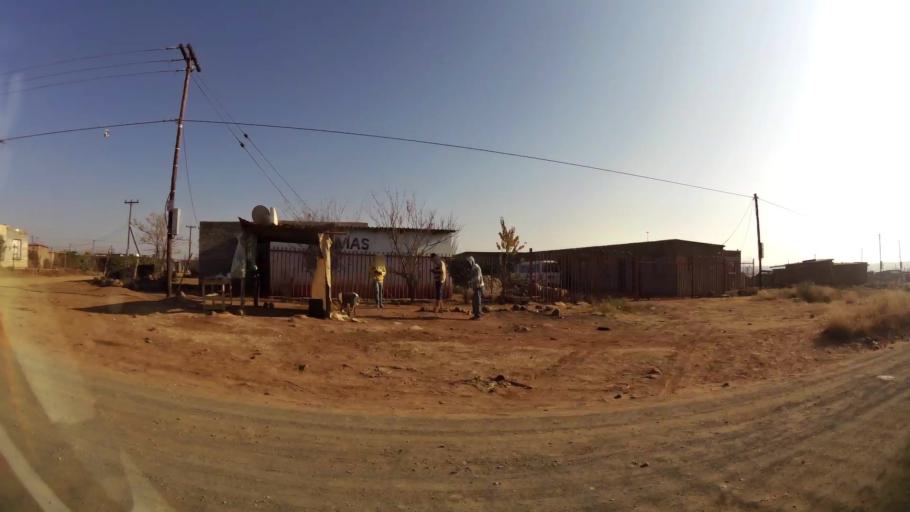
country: ZA
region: Orange Free State
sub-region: Mangaung Metropolitan Municipality
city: Bloemfontein
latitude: -29.2030
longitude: 26.2529
